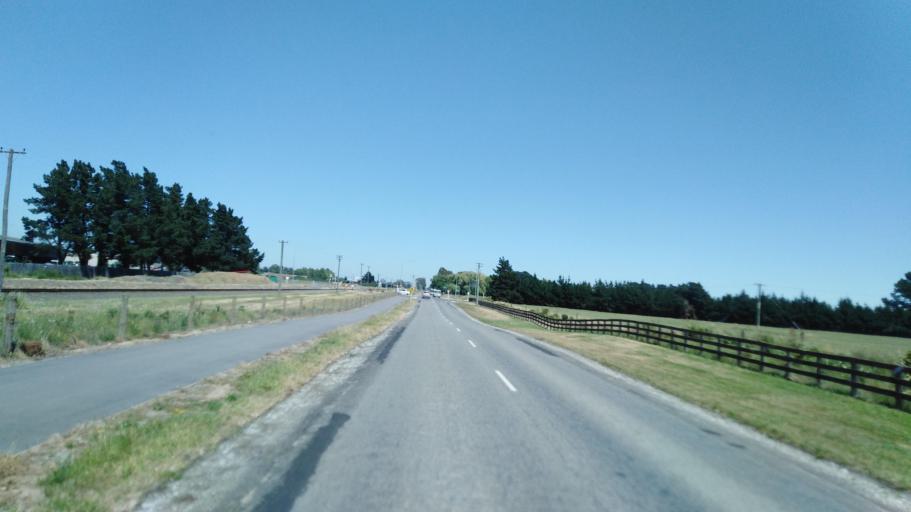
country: NZ
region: Canterbury
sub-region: Selwyn District
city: Rolleston
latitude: -43.5650
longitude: 172.4454
